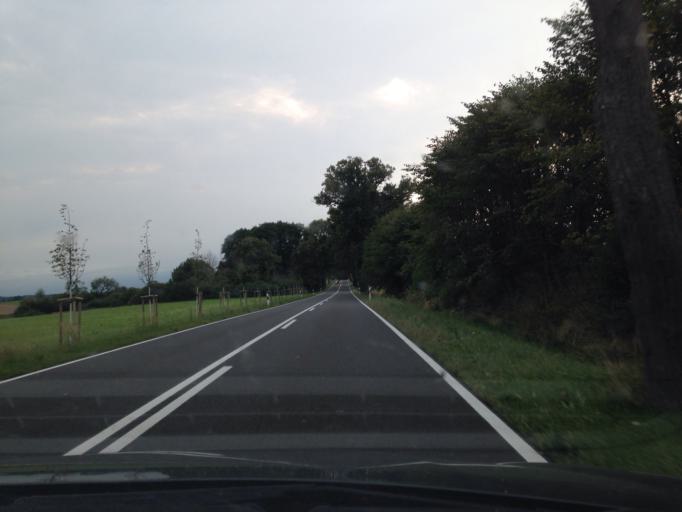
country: DE
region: Mecklenburg-Vorpommern
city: Blankensee
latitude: 53.3726
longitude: 13.2963
